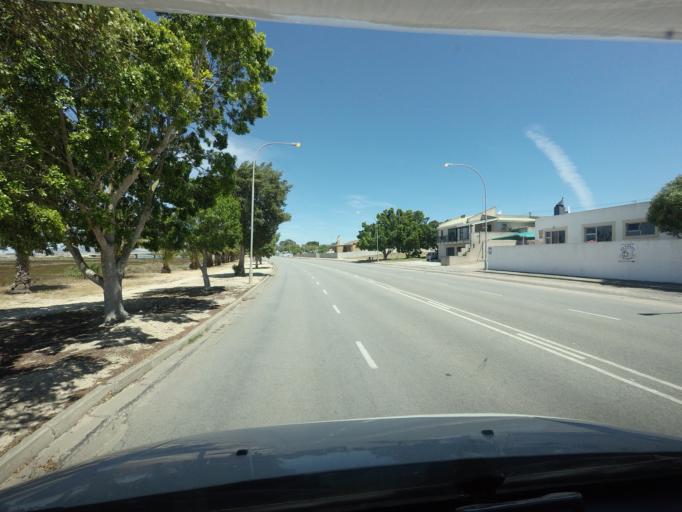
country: ZA
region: Western Cape
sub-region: West Coast District Municipality
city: Vredenburg
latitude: -32.7864
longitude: 18.1735
